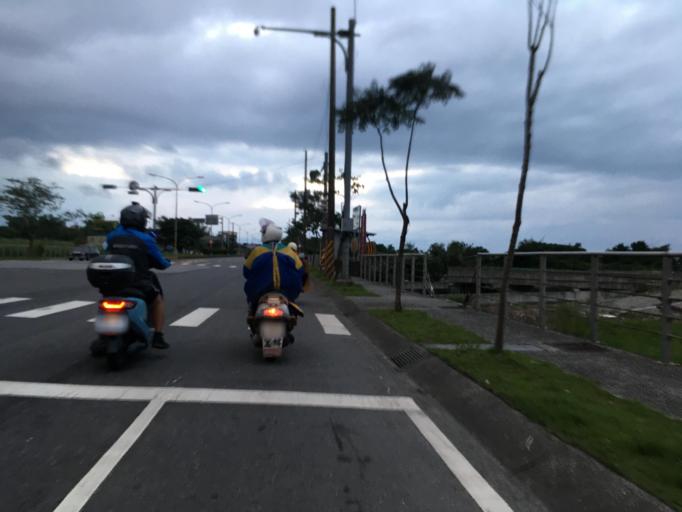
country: TW
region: Taiwan
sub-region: Yilan
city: Yilan
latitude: 24.6173
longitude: 121.8464
